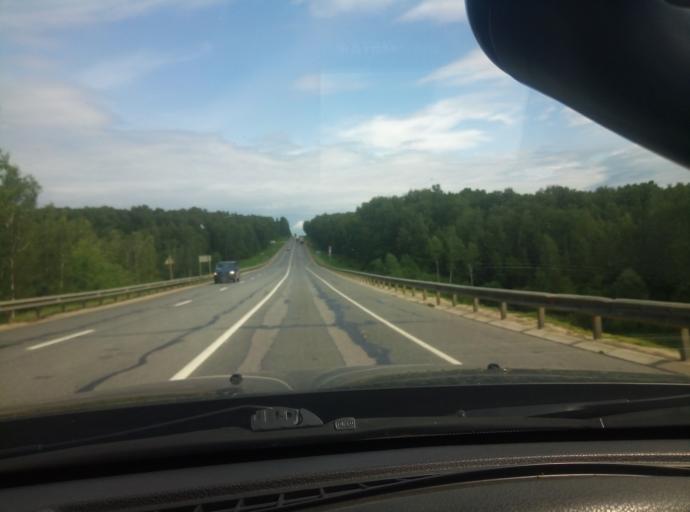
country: RU
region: Tula
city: Barsuki
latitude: 54.2745
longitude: 37.5352
